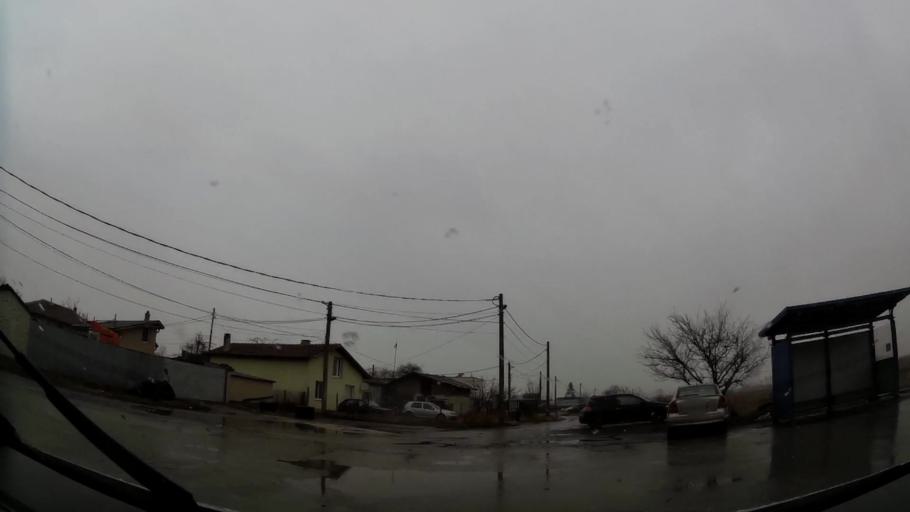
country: BG
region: Sofia-Capital
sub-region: Stolichna Obshtina
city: Sofia
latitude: 42.6636
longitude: 23.4279
